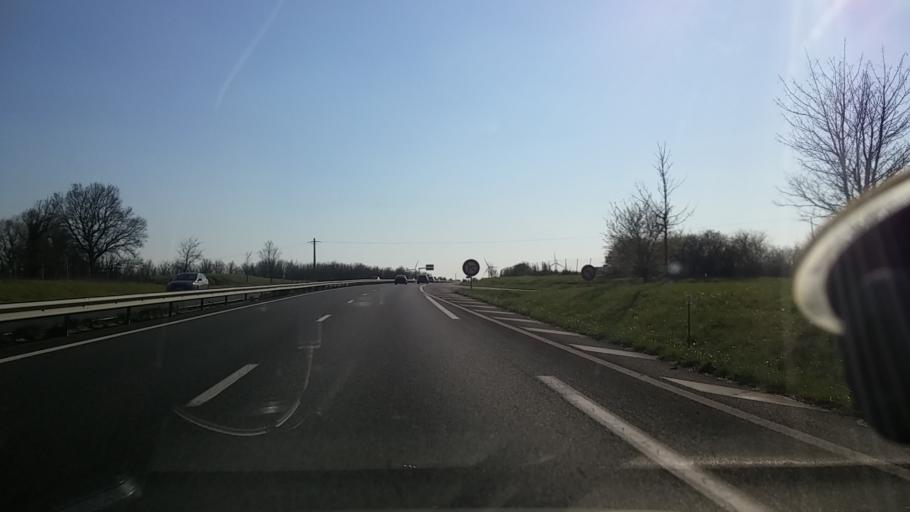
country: FR
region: Centre
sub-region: Departement du Cher
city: Massay
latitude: 47.1429
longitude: 1.9687
